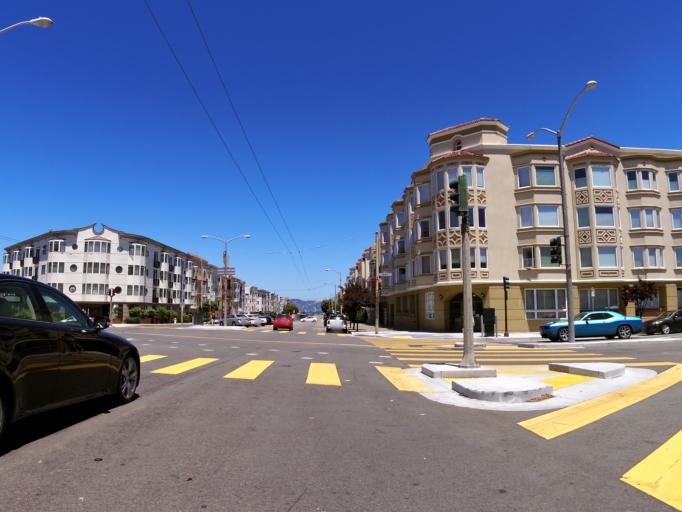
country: US
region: California
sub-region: San Francisco County
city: San Francisco
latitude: 37.8026
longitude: -122.4366
